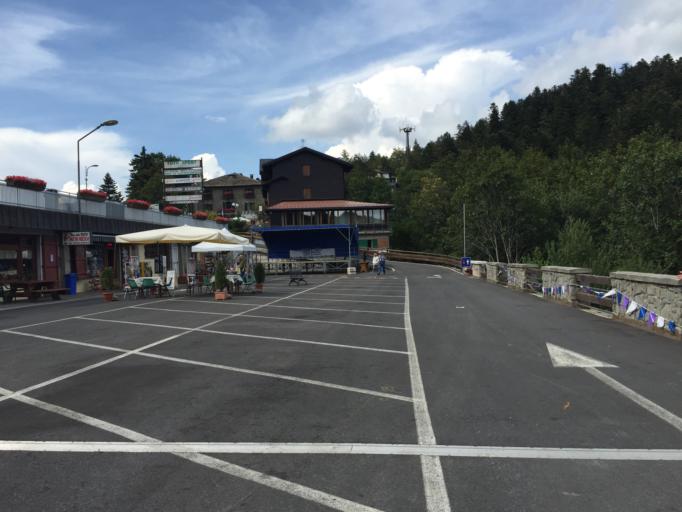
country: IT
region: Tuscany
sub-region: Provincia di Pistoia
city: Abetone
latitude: 44.1450
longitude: 10.6655
